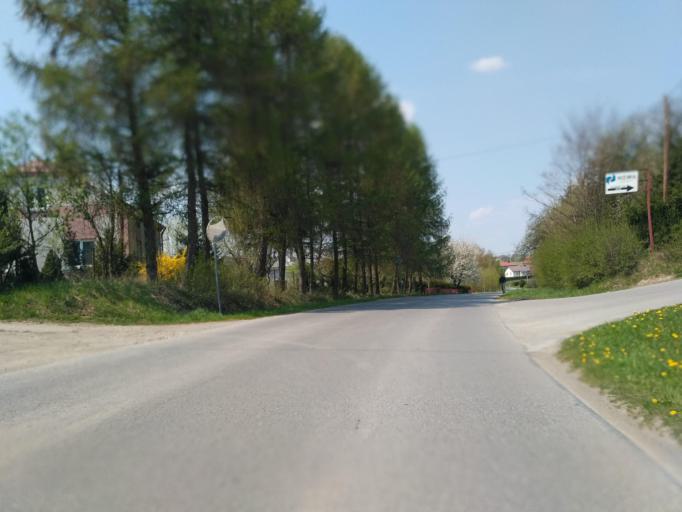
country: PL
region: Subcarpathian Voivodeship
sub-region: Powiat jasielski
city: Tarnowiec
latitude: 49.6709
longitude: 21.5485
